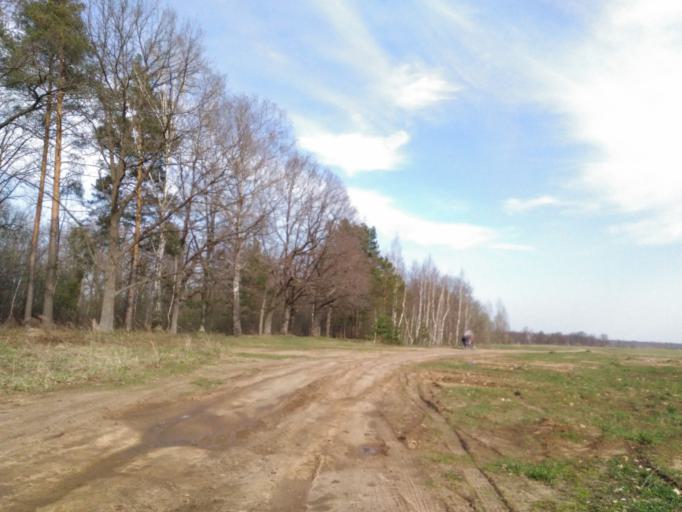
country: RU
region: Vladimir
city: Petushki
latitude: 55.9024
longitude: 39.4659
